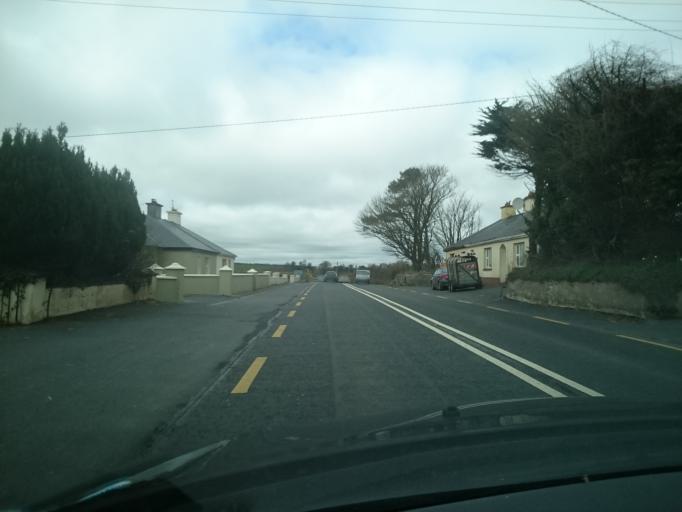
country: IE
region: Connaught
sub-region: Maigh Eo
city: Castlebar
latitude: 53.8141
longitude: -9.1563
